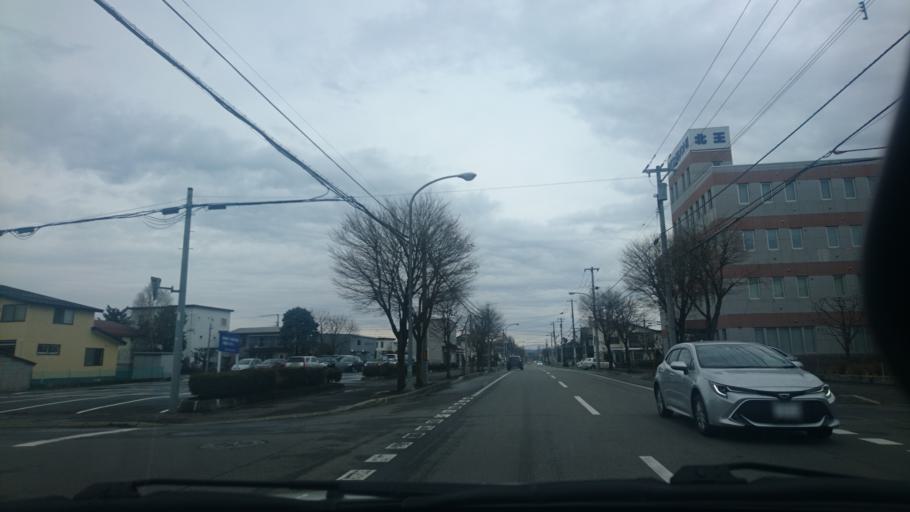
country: JP
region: Hokkaido
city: Obihiro
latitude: 42.9318
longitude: 143.1929
